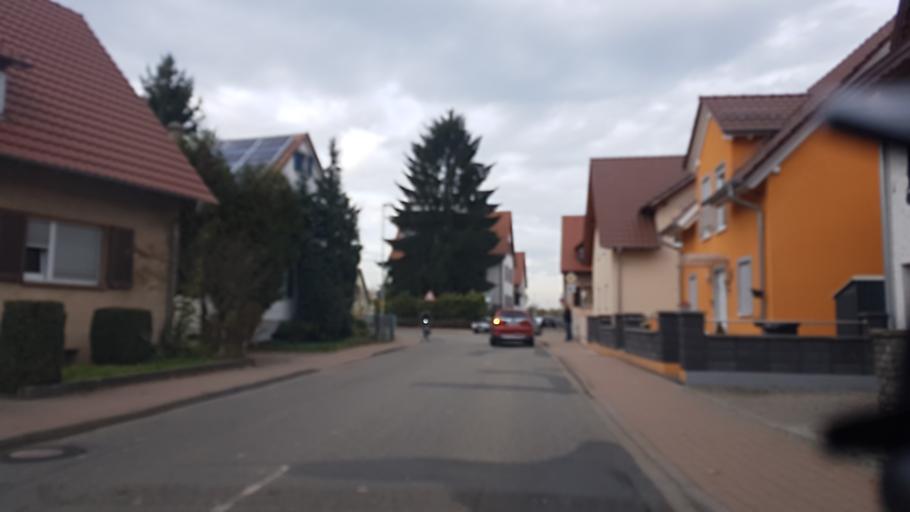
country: DE
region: Baden-Wuerttemberg
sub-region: Freiburg Region
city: Umkirch
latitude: 48.0637
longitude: 7.7795
